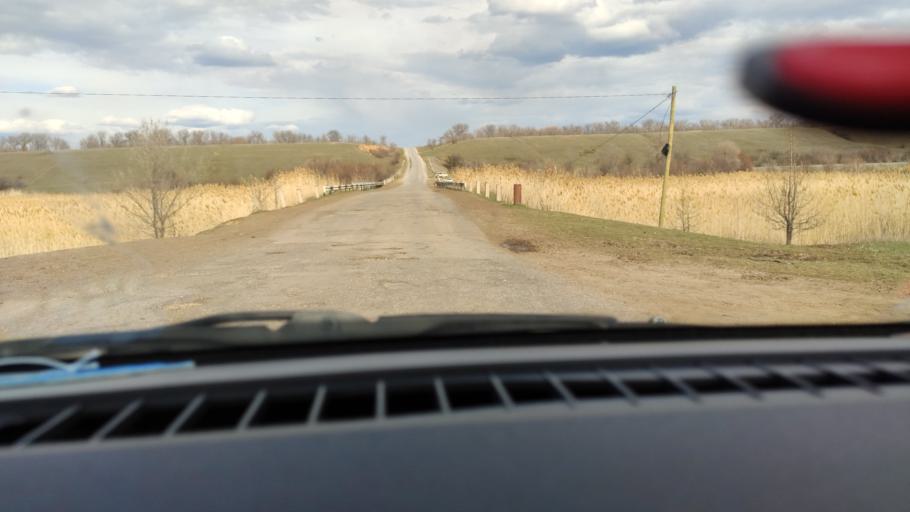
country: RU
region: Saratov
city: Rovnoye
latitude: 50.9391
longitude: 46.1145
